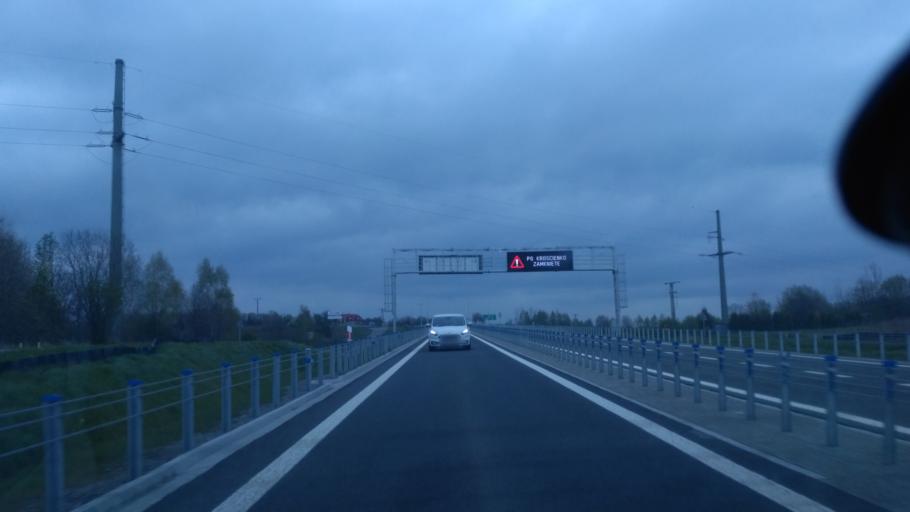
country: PL
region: Subcarpathian Voivodeship
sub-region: Powiat sanocki
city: Sanok
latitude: 49.5391
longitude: 22.2168
